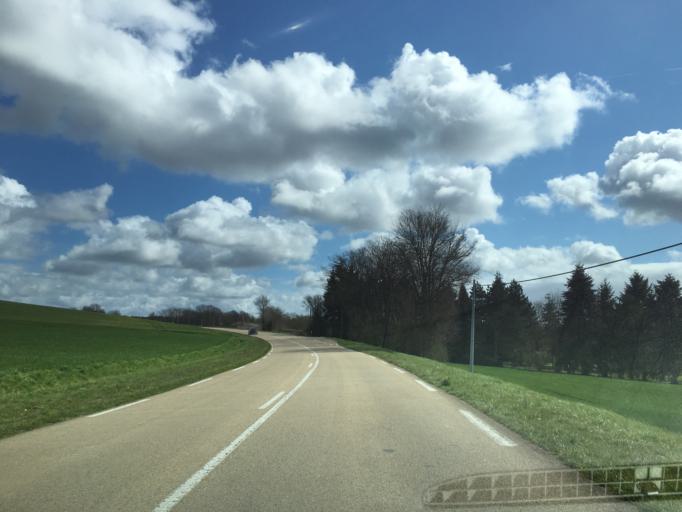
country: FR
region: Bourgogne
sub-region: Departement de l'Yonne
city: Charbuy
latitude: 47.8245
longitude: 3.4247
